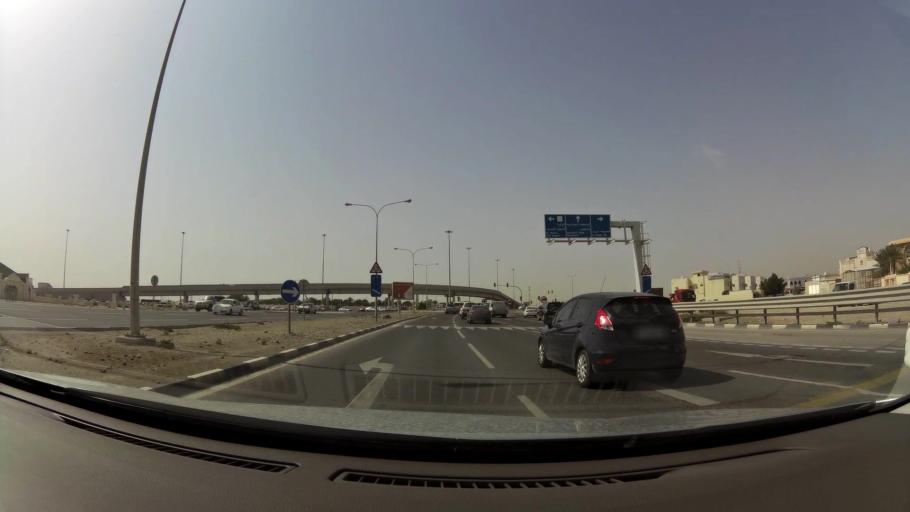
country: QA
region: Baladiyat ad Dawhah
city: Doha
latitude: 25.2390
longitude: 51.5234
